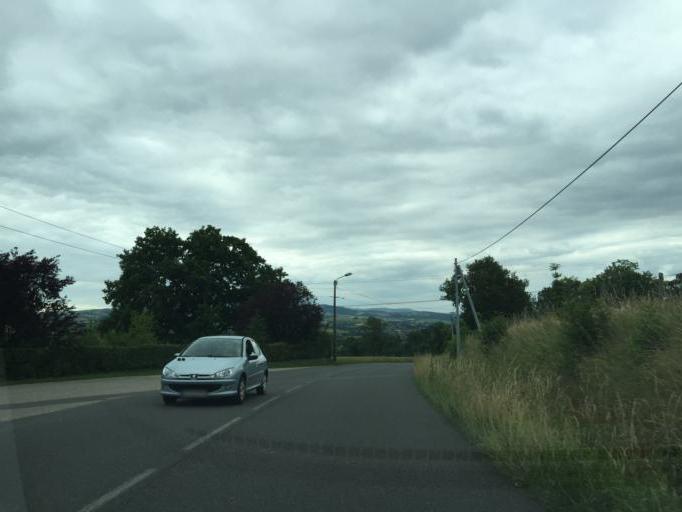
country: FR
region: Rhone-Alpes
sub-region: Departement de la Loire
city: Saint-Jean-Bonnefonds
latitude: 45.4438
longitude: 4.4760
